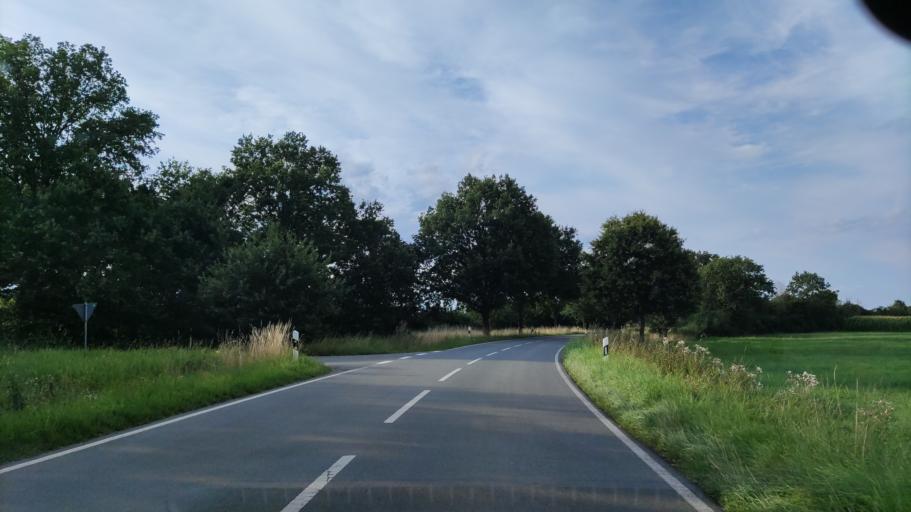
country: DE
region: Lower Saxony
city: Dannenberg
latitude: 53.1210
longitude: 11.1134
